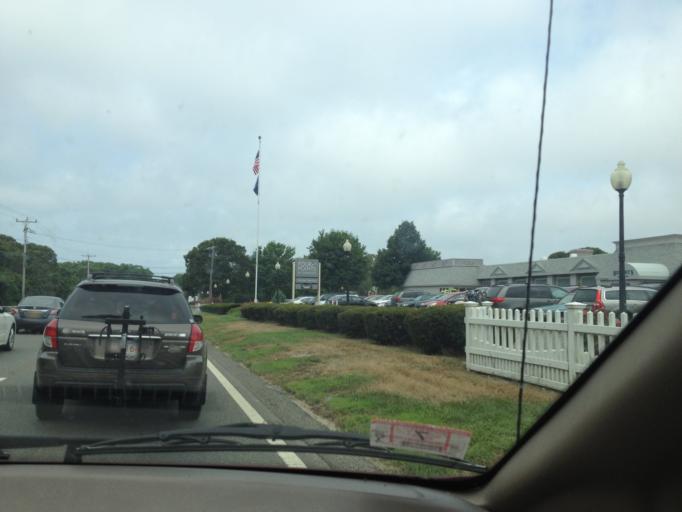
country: US
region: Massachusetts
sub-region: Barnstable County
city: North Eastham
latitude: 41.8462
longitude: -69.9855
